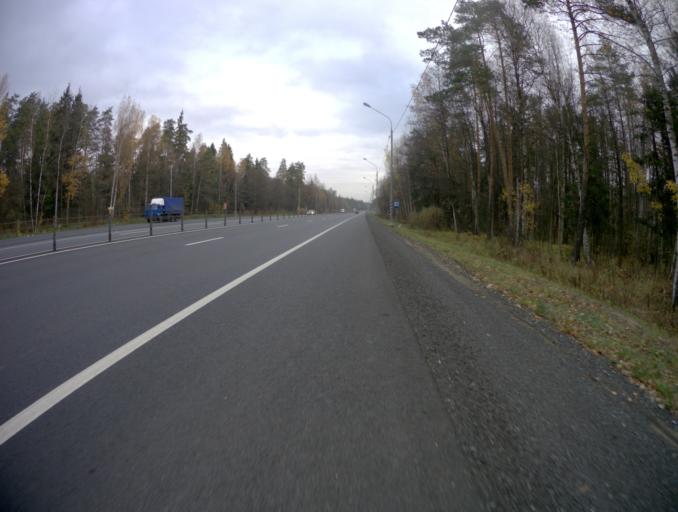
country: RU
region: Moskovskaya
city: Malaya Dubna
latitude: 55.8569
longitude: 38.9625
